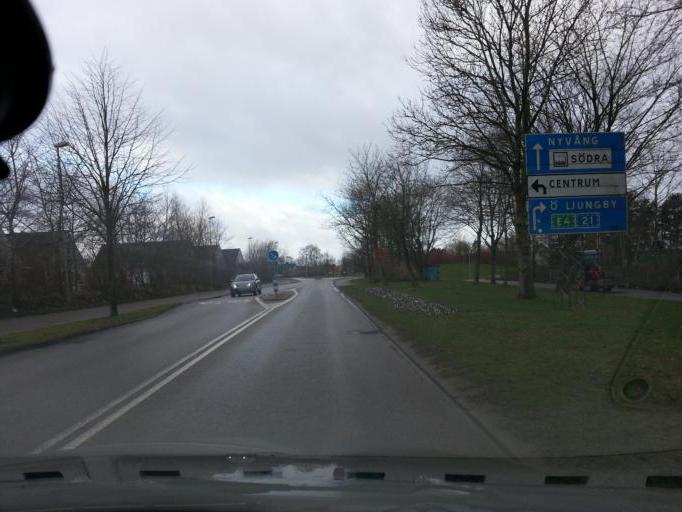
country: SE
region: Skane
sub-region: Astorps Kommun
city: Astorp
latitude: 56.1386
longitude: 12.9448
